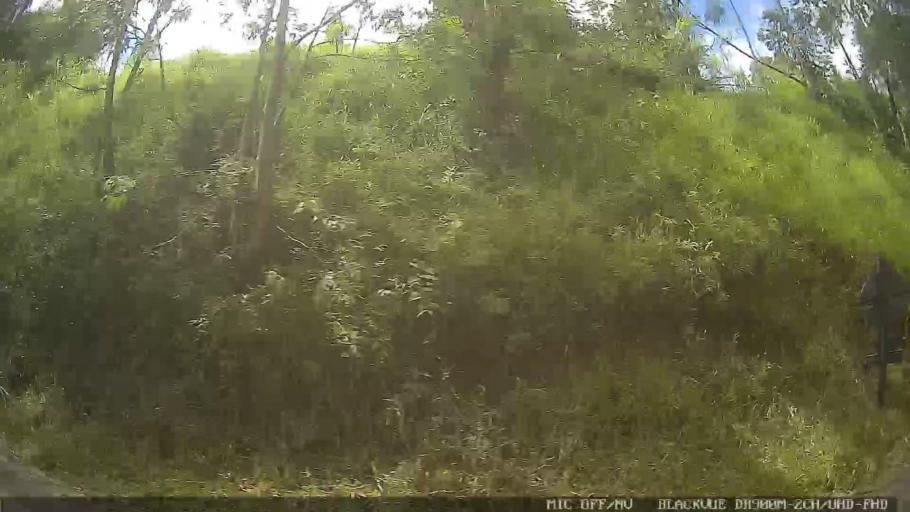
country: BR
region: Sao Paulo
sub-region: Braganca Paulista
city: Braganca Paulista
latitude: -22.8014
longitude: -46.5153
